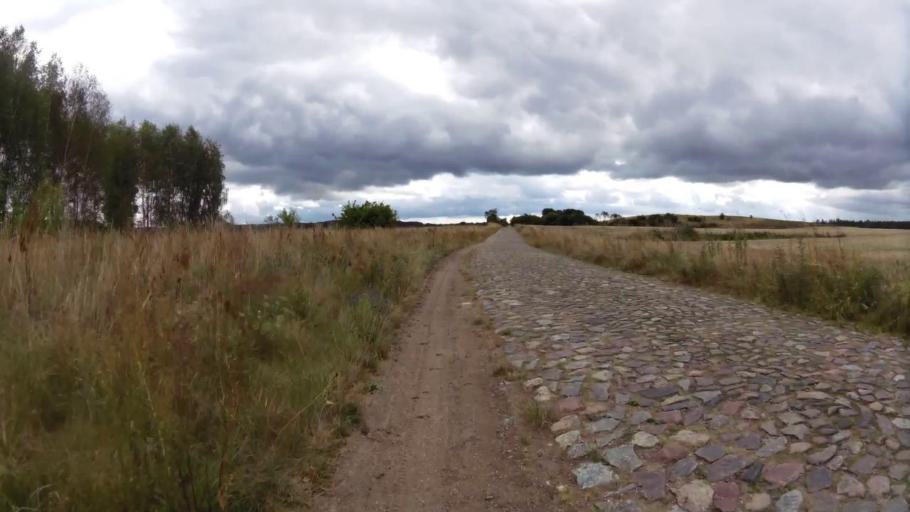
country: PL
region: West Pomeranian Voivodeship
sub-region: Powiat mysliborski
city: Debno
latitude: 52.8361
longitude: 14.7165
